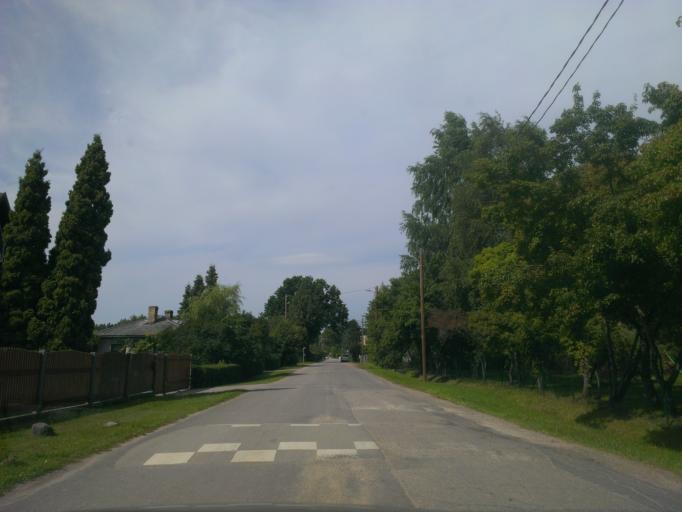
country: LV
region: Baldone
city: Baldone
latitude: 56.7442
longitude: 24.3908
